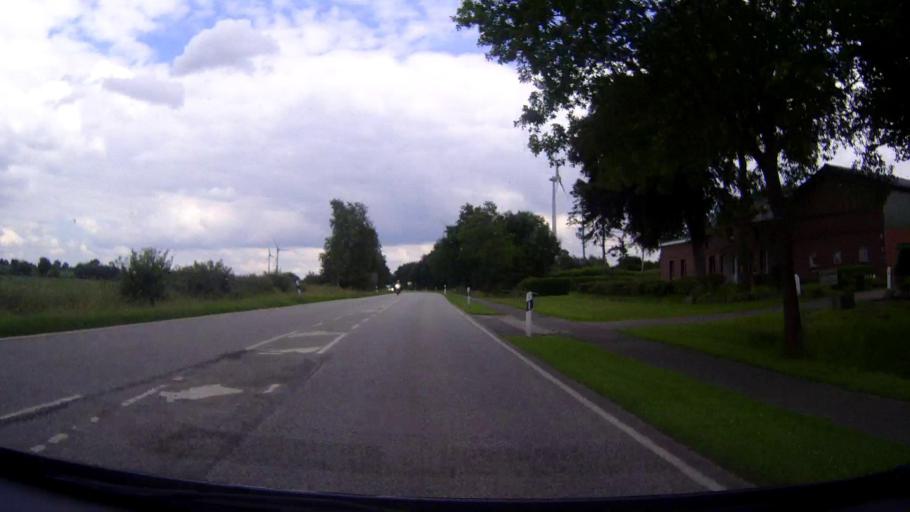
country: DE
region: Schleswig-Holstein
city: Beldorf
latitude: 54.1213
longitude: 9.3435
